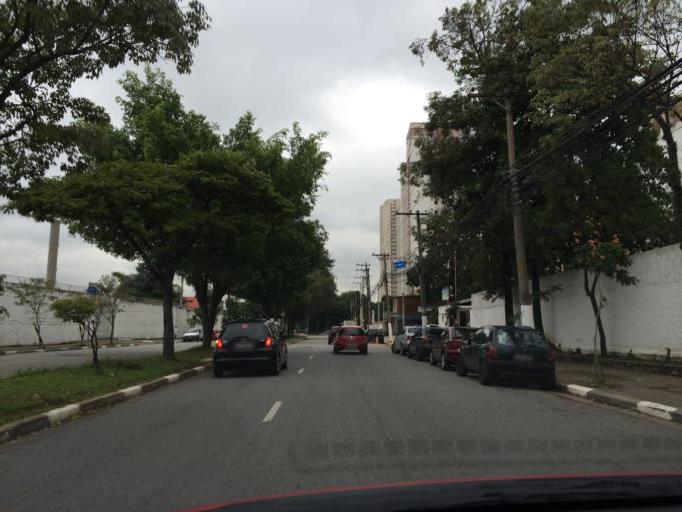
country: BR
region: Sao Paulo
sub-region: Osasco
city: Osasco
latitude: -23.5518
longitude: -46.7395
